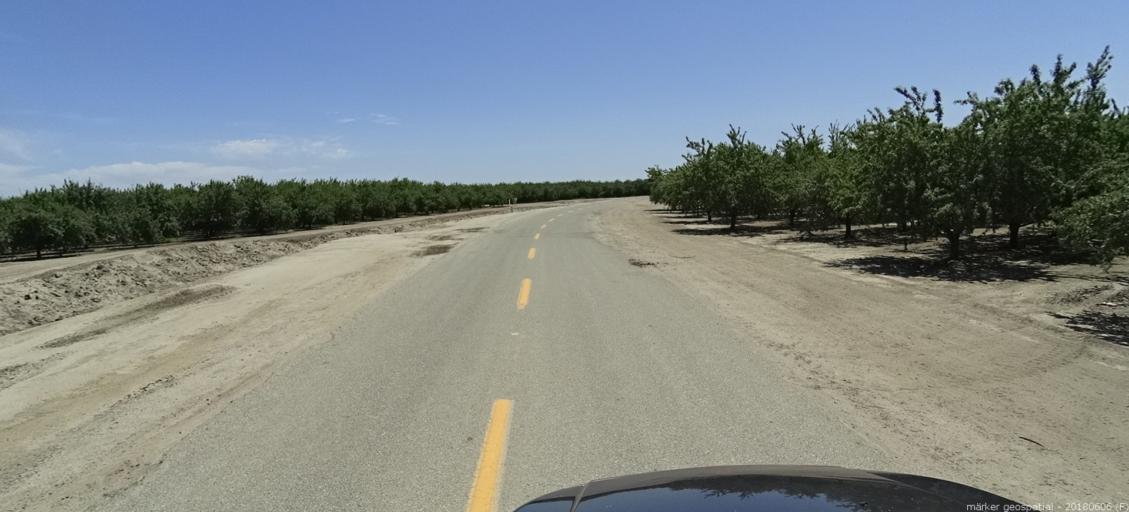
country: US
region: California
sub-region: Fresno County
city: Mendota
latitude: 36.8156
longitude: -120.3659
